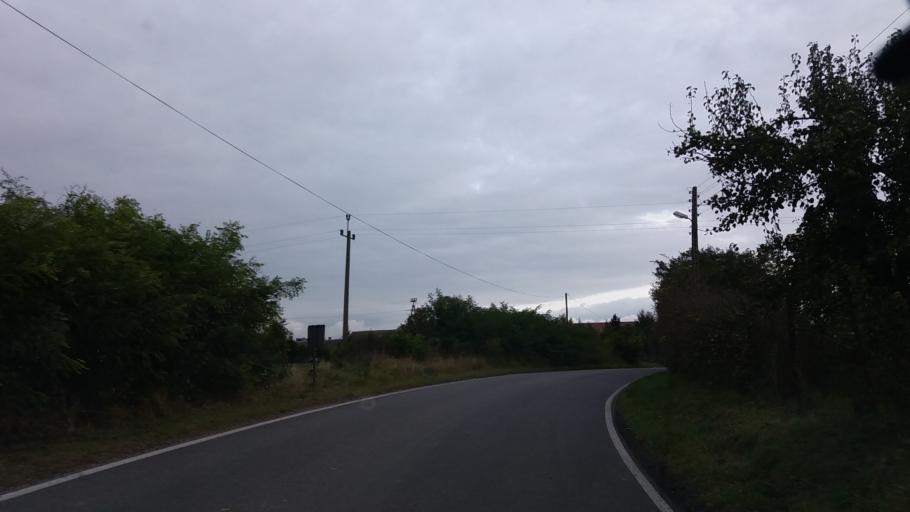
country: PL
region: West Pomeranian Voivodeship
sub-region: Powiat choszczenski
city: Pelczyce
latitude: 53.0261
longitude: 15.3642
